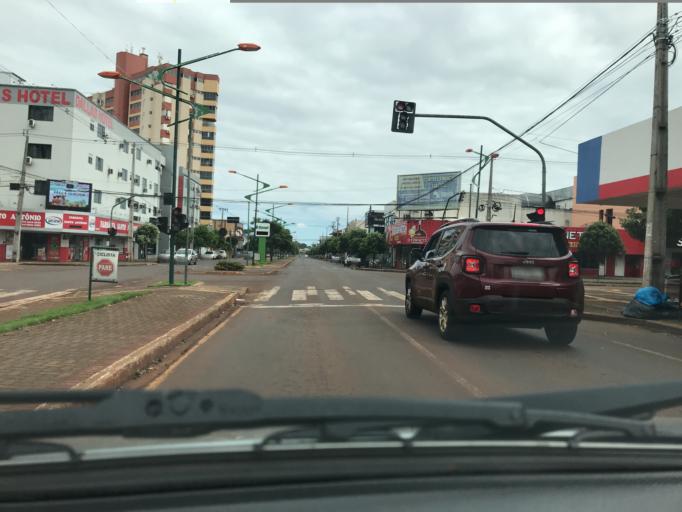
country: BR
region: Parana
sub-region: Palotina
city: Palotina
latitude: -24.2835
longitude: -53.8398
